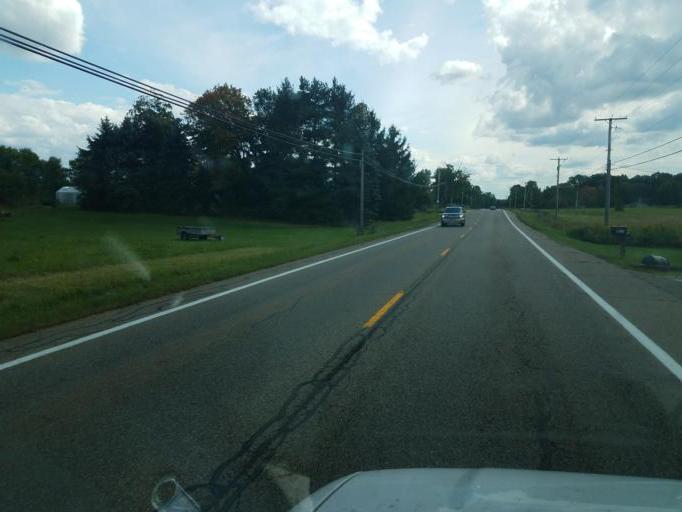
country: US
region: Ohio
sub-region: Portage County
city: Ravenna
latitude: 41.0728
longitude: -81.2434
